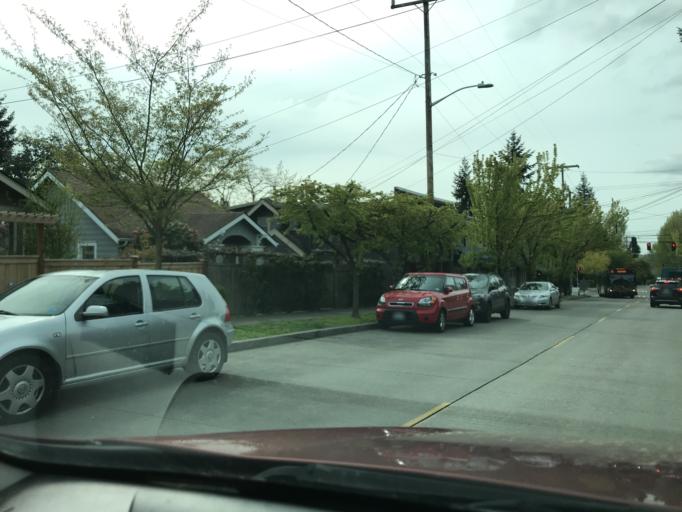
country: US
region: Washington
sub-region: King County
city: Seattle
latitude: 47.6695
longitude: -122.2902
